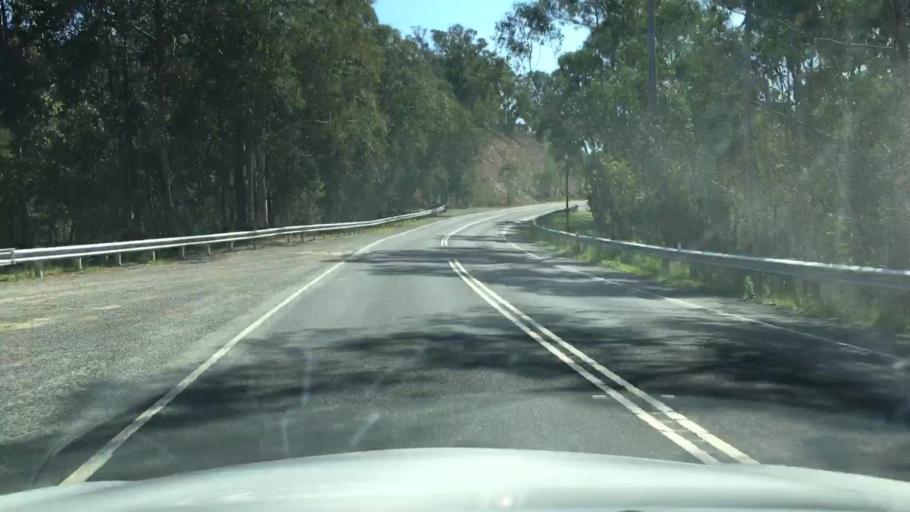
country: AU
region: Victoria
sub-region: Nillumbik
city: Saint Andrews
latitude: -37.6643
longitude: 145.2668
